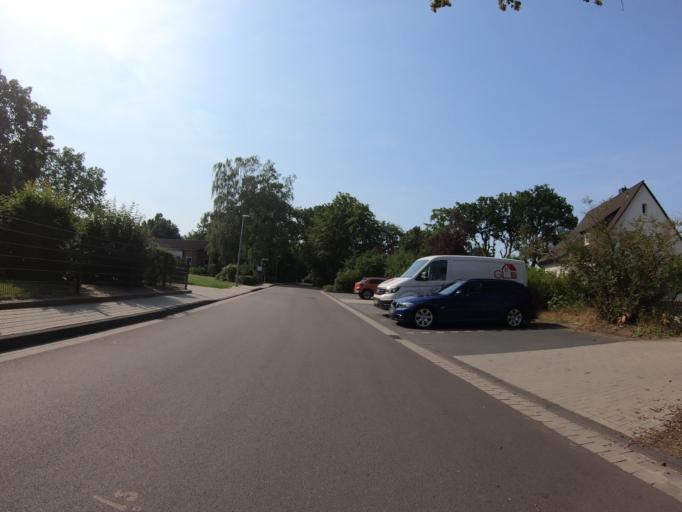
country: DE
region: Lower Saxony
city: Gifhorn
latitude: 52.4836
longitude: 10.5355
